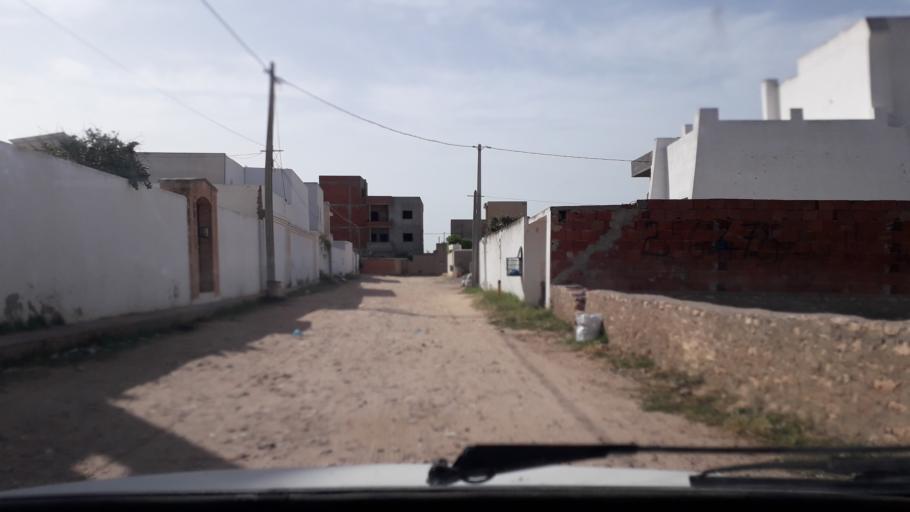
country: TN
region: Safaqis
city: Al Qarmadah
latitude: 34.8080
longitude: 10.7711
